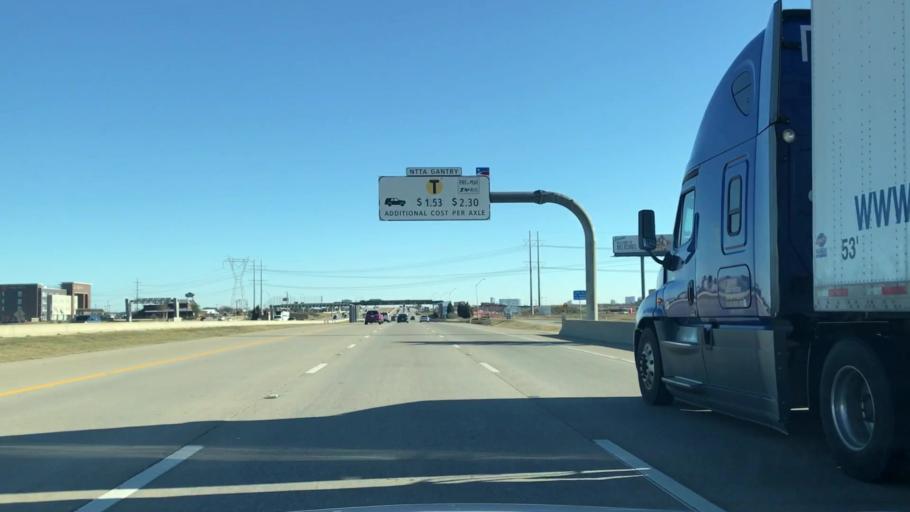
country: US
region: Texas
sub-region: Denton County
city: The Colony
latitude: 33.0605
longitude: -96.9001
